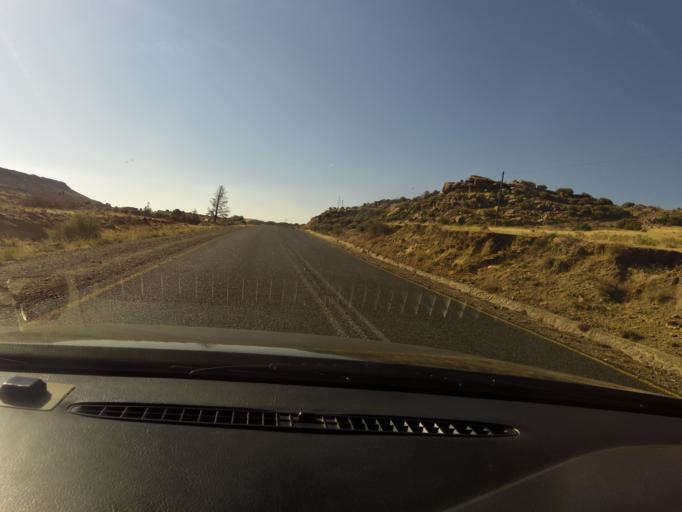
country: LS
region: Mohale's Hoek District
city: Mohale's Hoek
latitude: -30.0807
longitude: 27.4281
